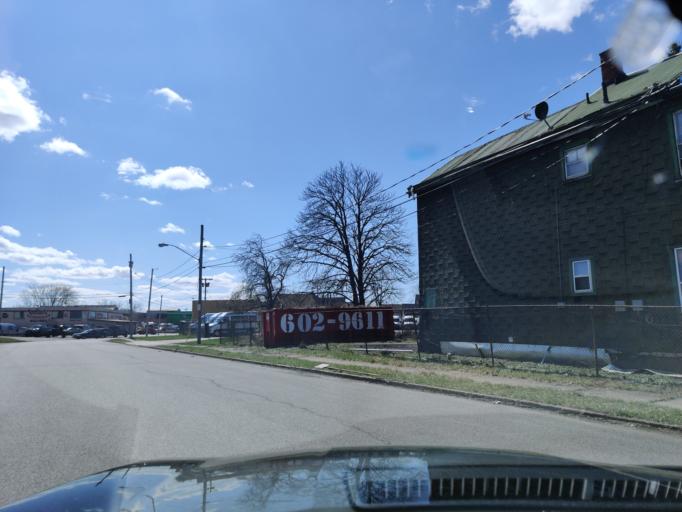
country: US
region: New York
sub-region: Erie County
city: Sloan
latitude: 42.8848
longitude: -78.8299
